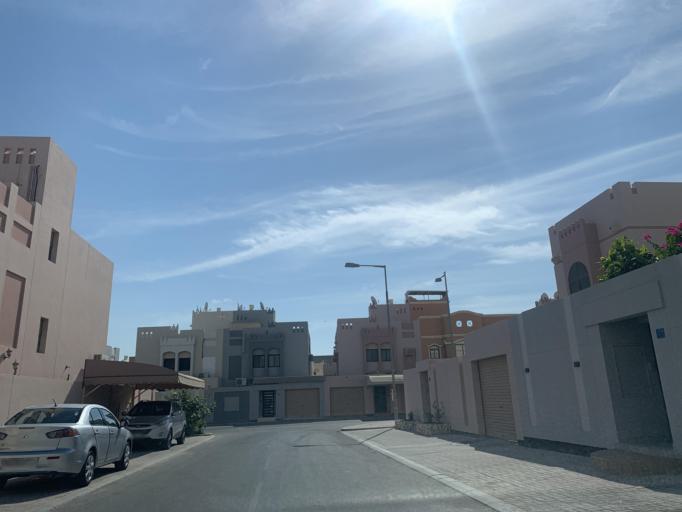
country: BH
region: Central Governorate
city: Madinat Hamad
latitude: 26.1174
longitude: 50.4860
